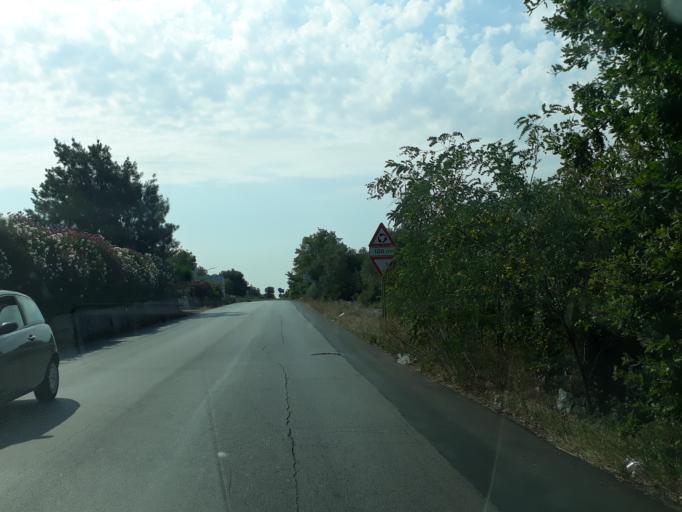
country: IT
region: Apulia
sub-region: Provincia di Brindisi
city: Carovigno
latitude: 40.6970
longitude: 17.6673
